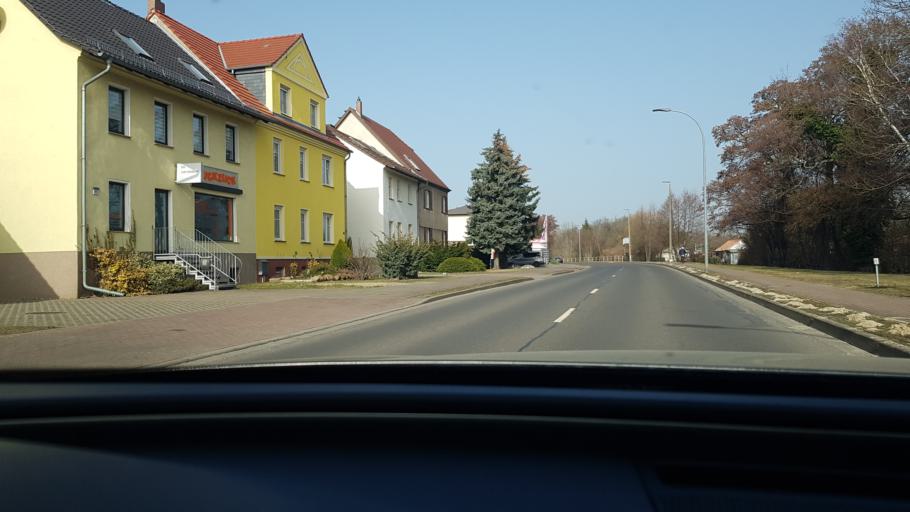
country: DE
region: Brandenburg
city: Guben
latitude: 51.9638
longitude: 14.7023
